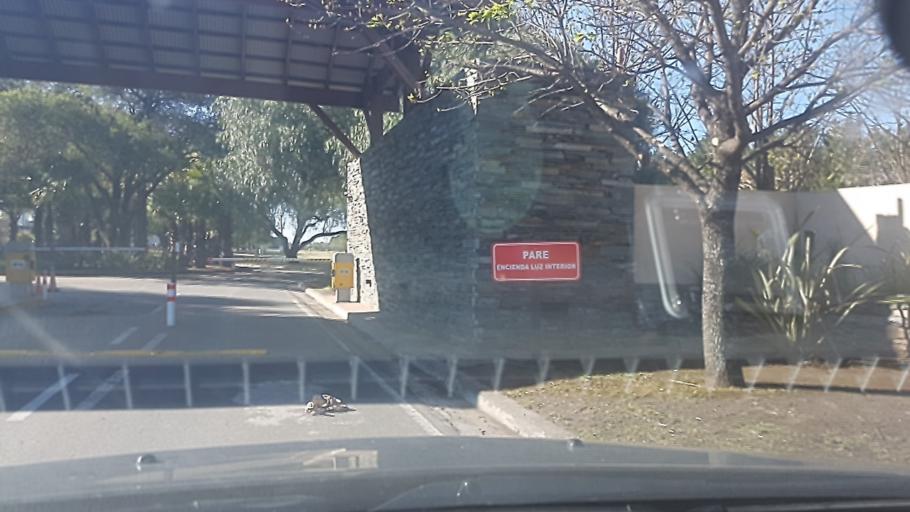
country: AR
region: Cordoba
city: Villa Allende
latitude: -31.3029
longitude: -64.2338
